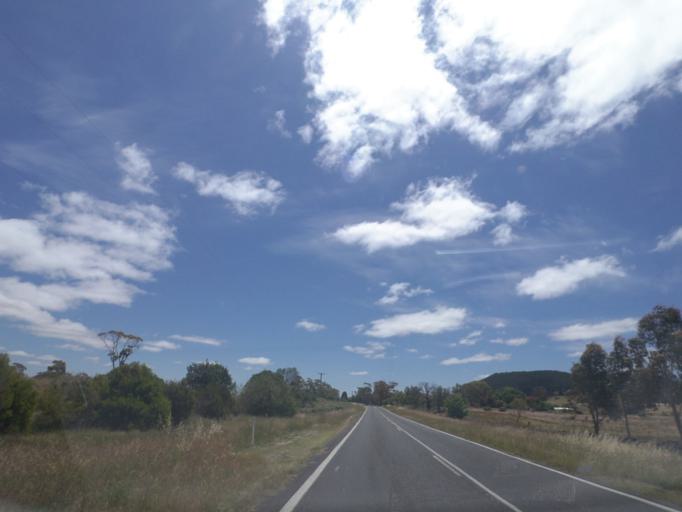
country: AU
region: Victoria
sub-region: Mount Alexander
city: Castlemaine
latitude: -37.2797
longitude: 144.1505
